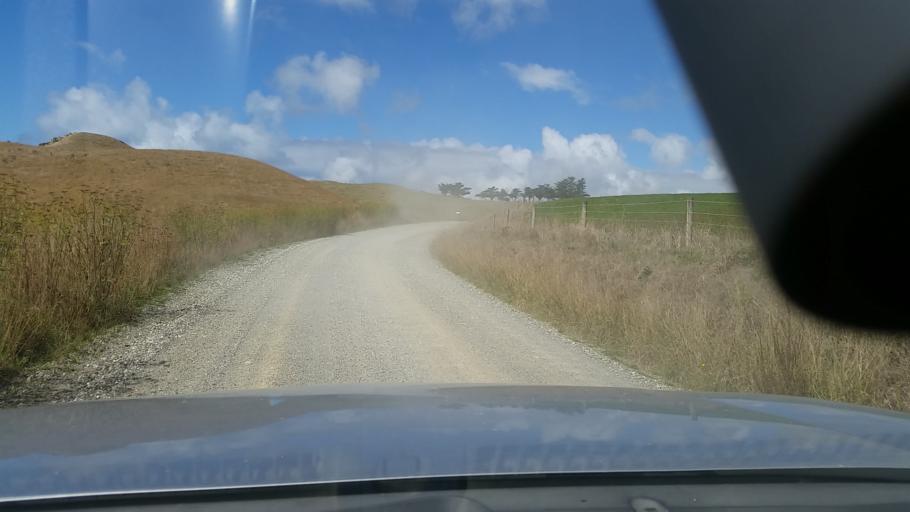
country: NZ
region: Marlborough
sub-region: Marlborough District
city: Blenheim
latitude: -41.6932
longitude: 174.1446
